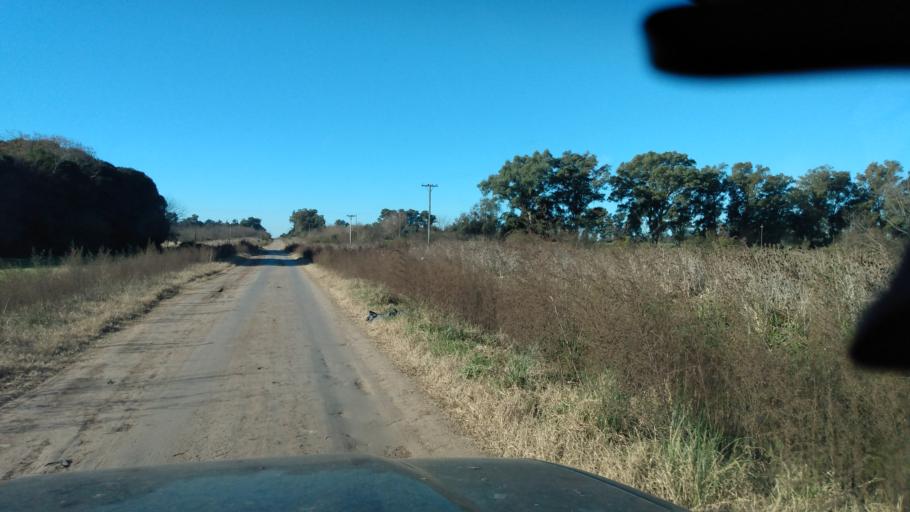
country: AR
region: Buenos Aires
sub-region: Partido de Lujan
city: Lujan
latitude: -34.5636
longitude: -59.1669
